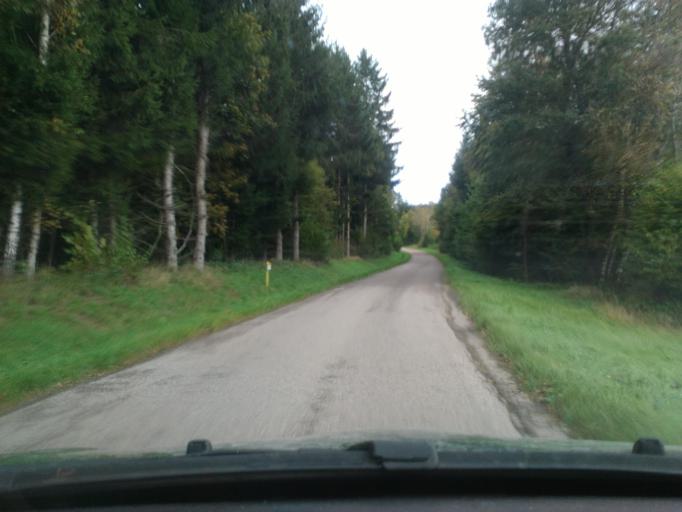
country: FR
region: Lorraine
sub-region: Departement des Vosges
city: Etival-Clairefontaine
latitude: 48.3420
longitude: 6.8554
